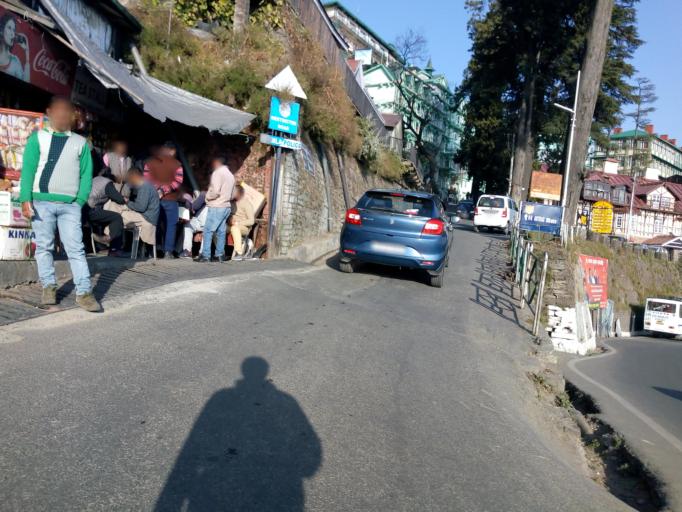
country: IN
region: Himachal Pradesh
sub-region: Shimla
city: Shimla
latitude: 31.1050
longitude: 77.1660
